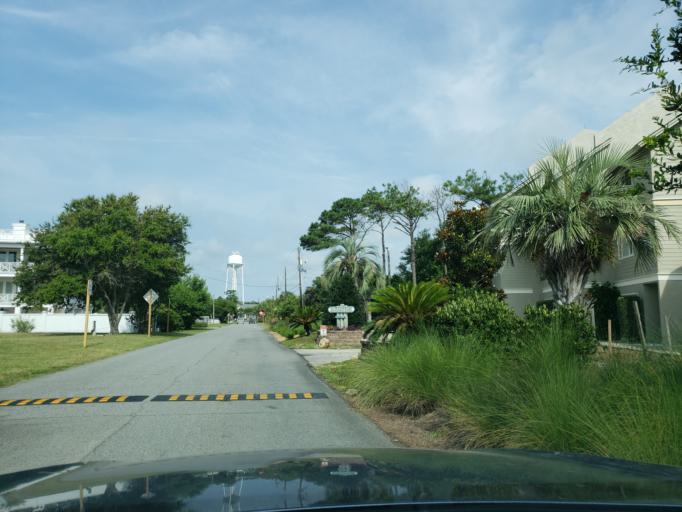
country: US
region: Georgia
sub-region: Chatham County
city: Tybee Island
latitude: 32.0234
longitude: -80.8457
